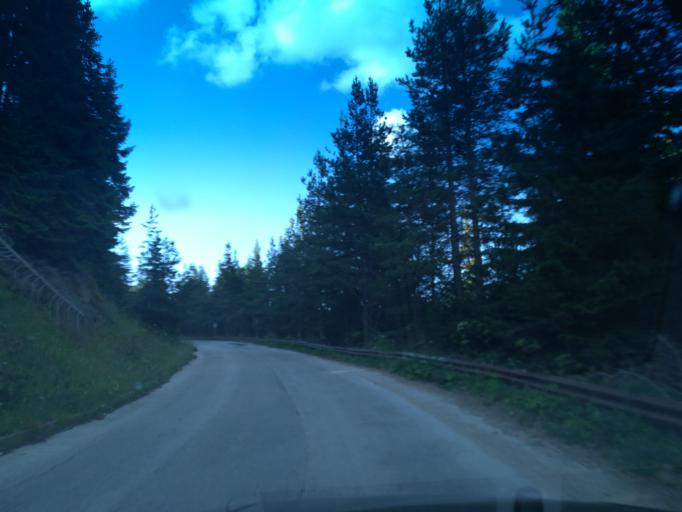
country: BG
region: Smolyan
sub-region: Obshtina Chepelare
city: Chepelare
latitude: 41.6896
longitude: 24.7577
